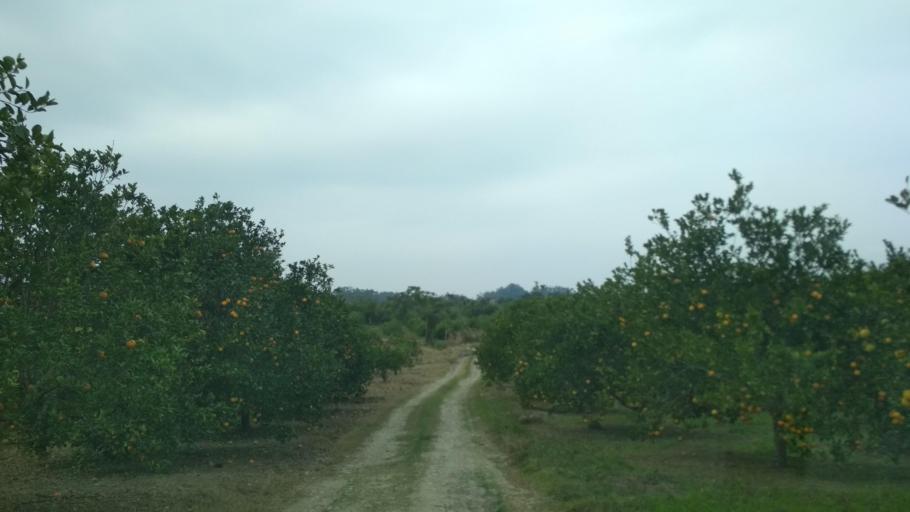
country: MM
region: Kayah
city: Loikaw
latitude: 20.2142
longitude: 97.3289
